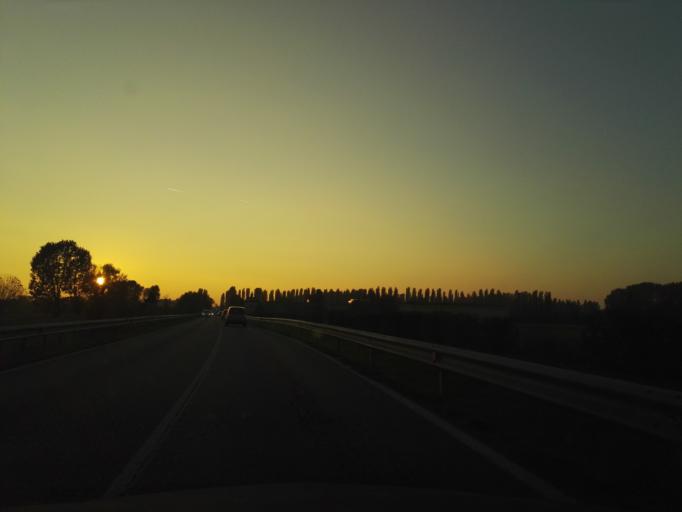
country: IT
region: Lombardy
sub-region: Citta metropolitana di Milano
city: Vigliano-Bettolino
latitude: 45.4343
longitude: 9.3300
